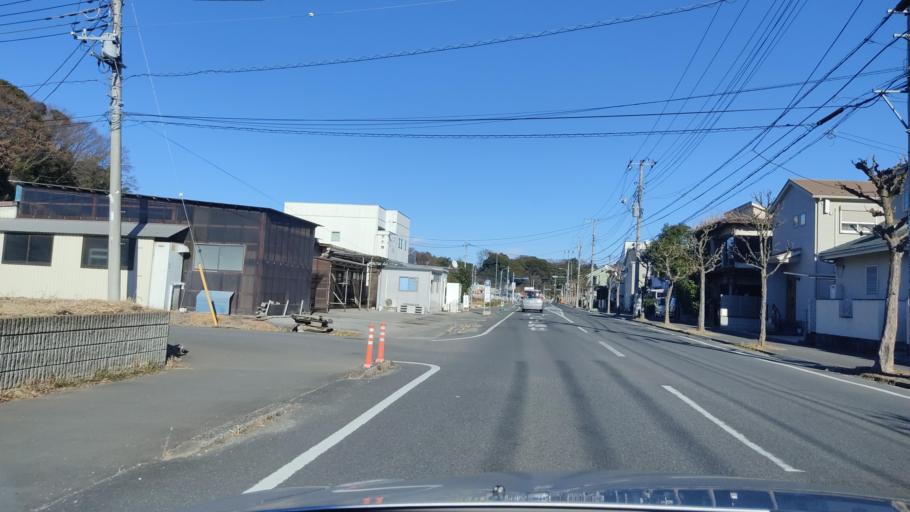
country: JP
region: Chiba
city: Nagareyama
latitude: 35.8494
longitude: 139.9176
